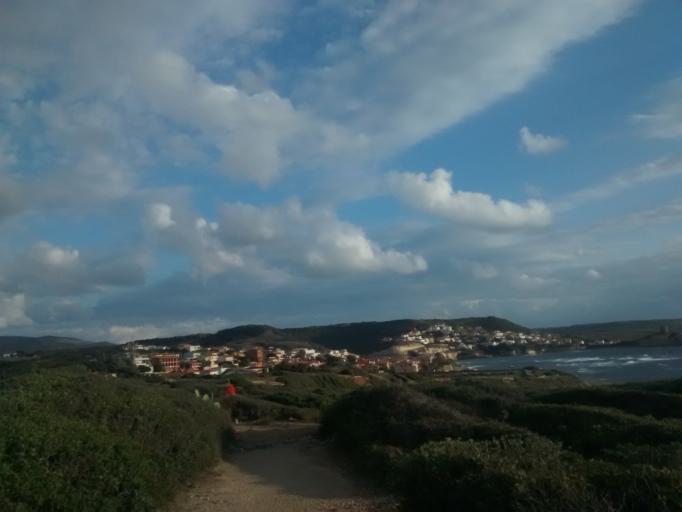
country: IT
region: Sardinia
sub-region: Provincia di Oristano
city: Narbolia
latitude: 40.0960
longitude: 8.4885
